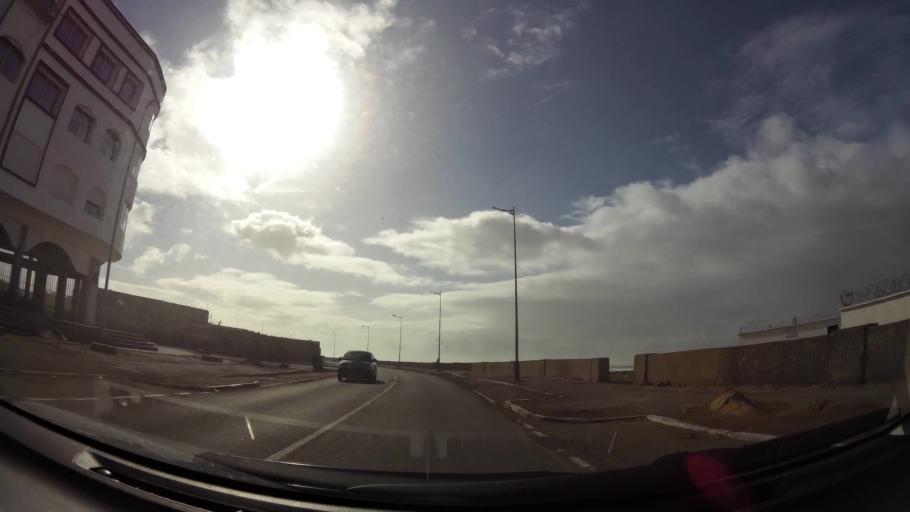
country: MA
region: Doukkala-Abda
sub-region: El-Jadida
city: El Jadida
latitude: 33.2638
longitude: -8.5096
